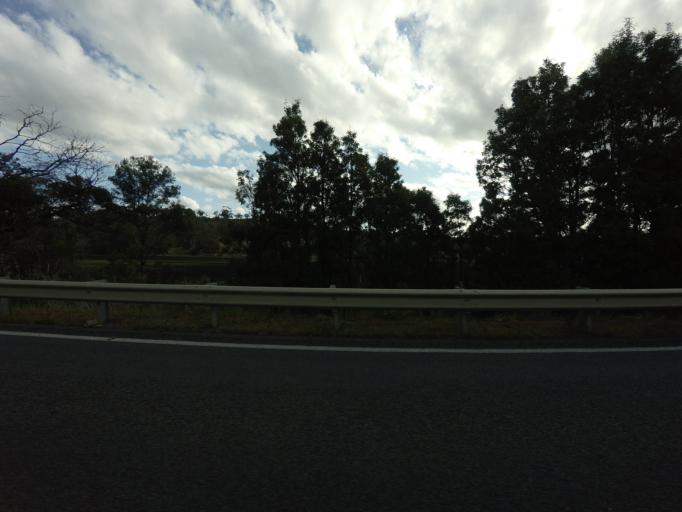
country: AU
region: Tasmania
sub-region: Sorell
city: Sorell
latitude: -42.7266
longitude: 147.5228
